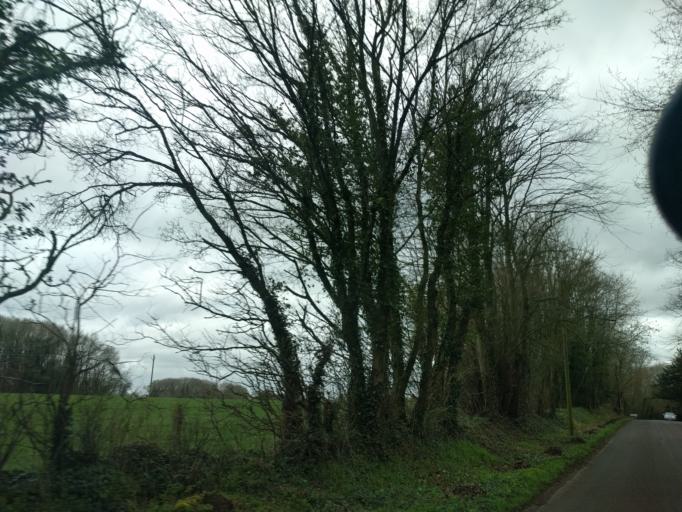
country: GB
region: England
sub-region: Wiltshire
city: Biddestone
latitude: 51.5146
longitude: -2.2032
